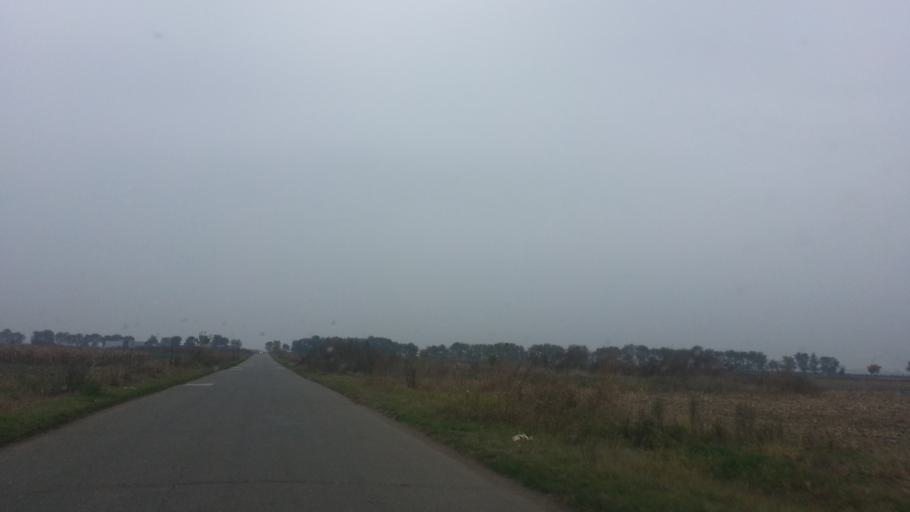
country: RS
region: Autonomna Pokrajina Vojvodina
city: Nova Pazova
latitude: 44.9576
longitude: 20.2180
